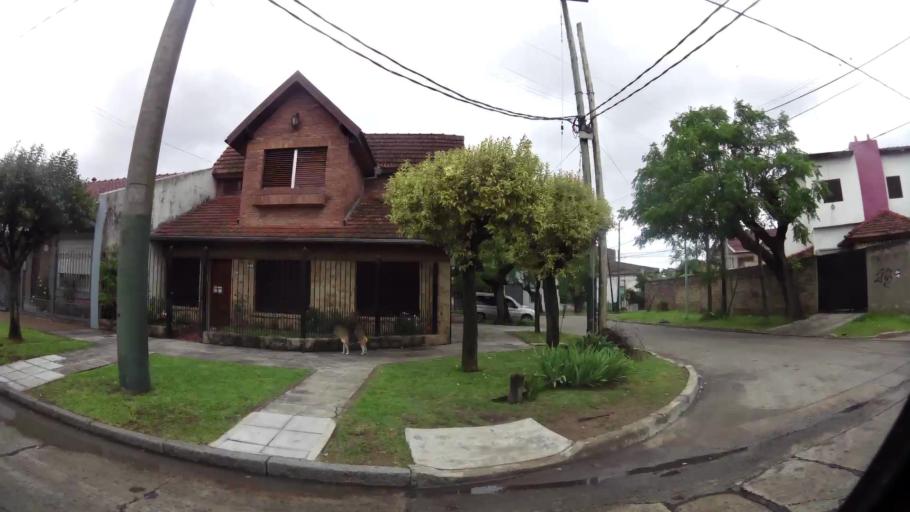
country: AR
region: Buenos Aires
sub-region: Partido de Lomas de Zamora
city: Lomas de Zamora
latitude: -34.7483
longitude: -58.3852
